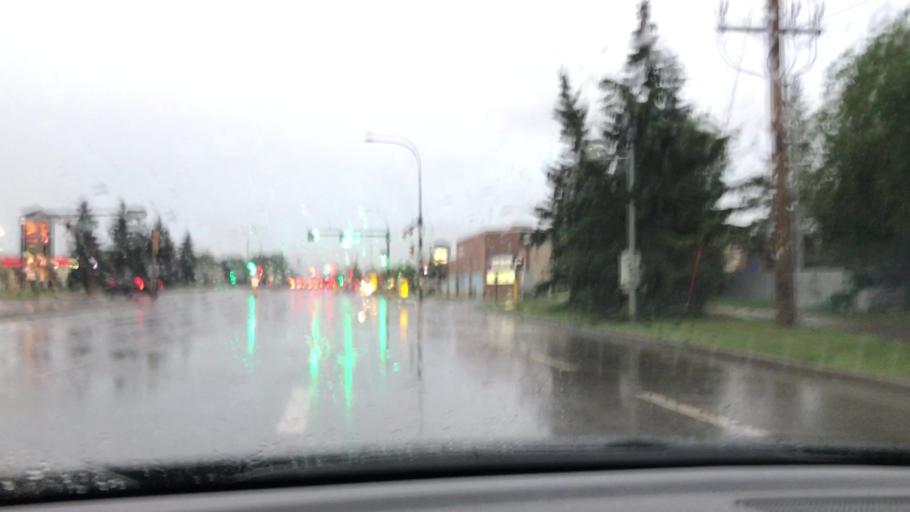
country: CA
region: Alberta
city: Sherwood Park
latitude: 53.5143
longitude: -113.3202
